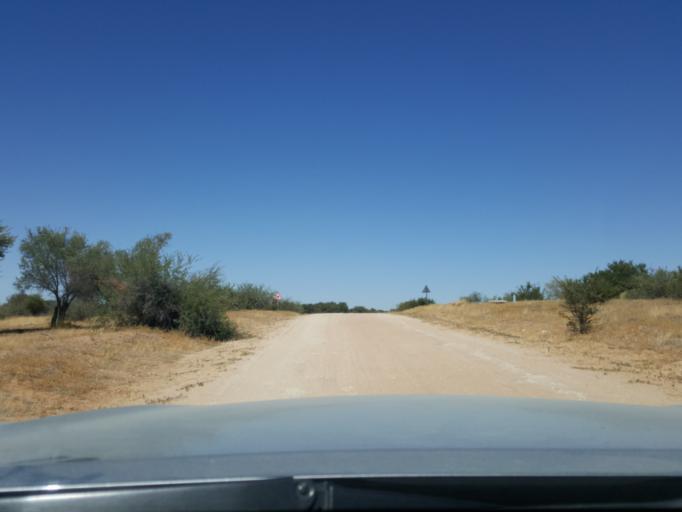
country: BW
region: Kgalagadi
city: Hukuntsi
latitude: -23.9809
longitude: 21.2081
